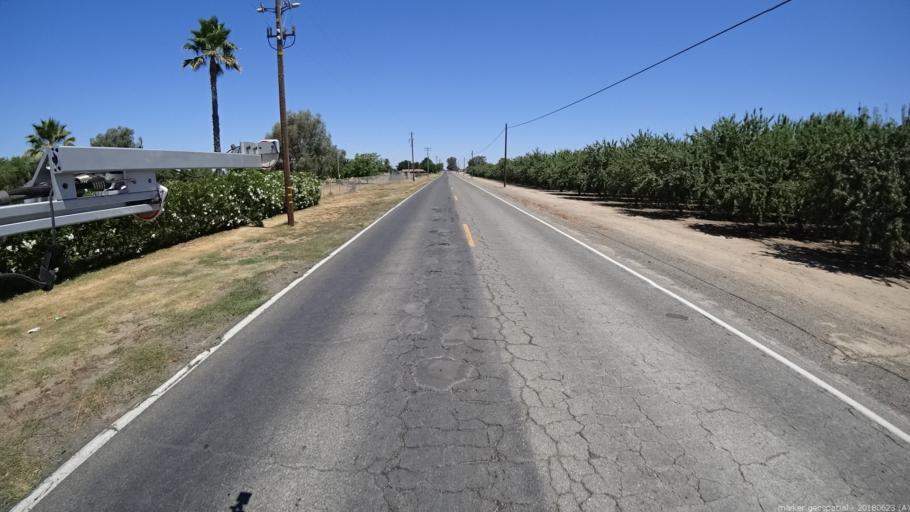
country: US
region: California
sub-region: Madera County
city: Chowchilla
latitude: 37.0962
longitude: -120.2568
